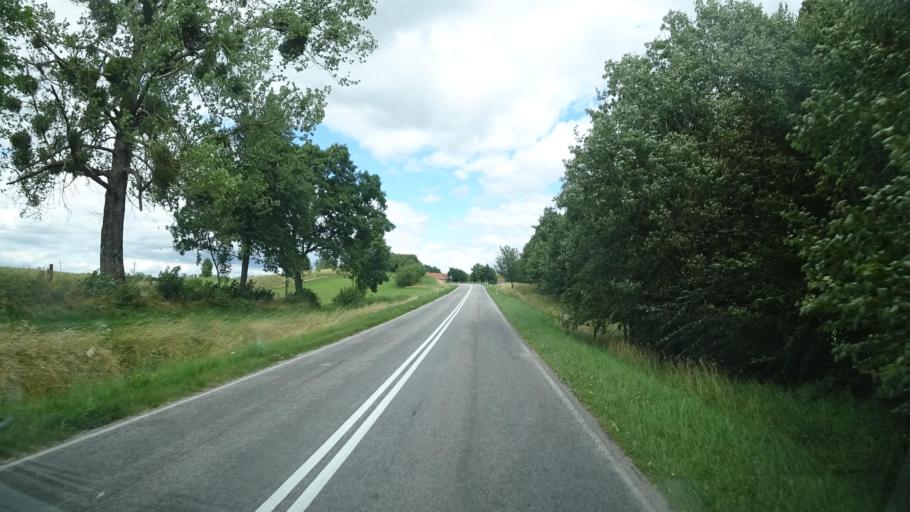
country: PL
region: Warmian-Masurian Voivodeship
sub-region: Powiat goldapski
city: Goldap
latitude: 54.2179
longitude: 22.2270
